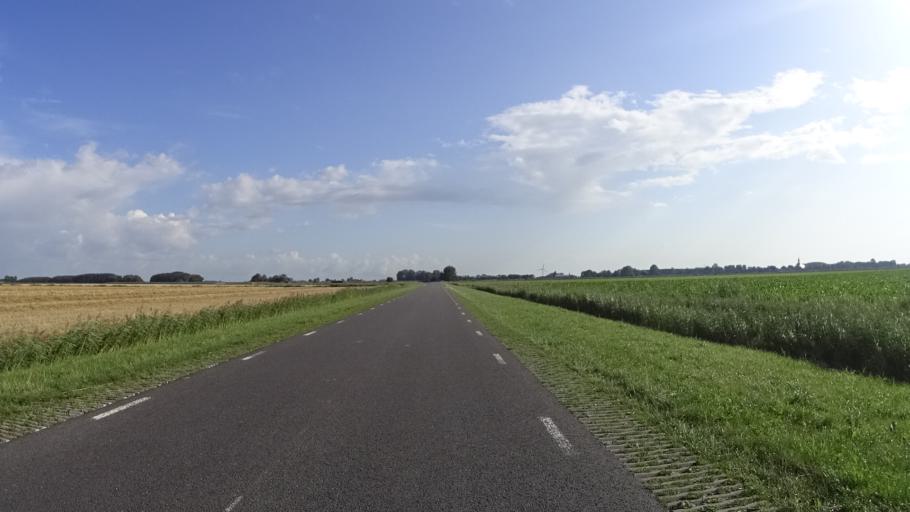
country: NL
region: Friesland
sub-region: Gemeente Harlingen
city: Harlingen
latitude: 53.1253
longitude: 5.4561
